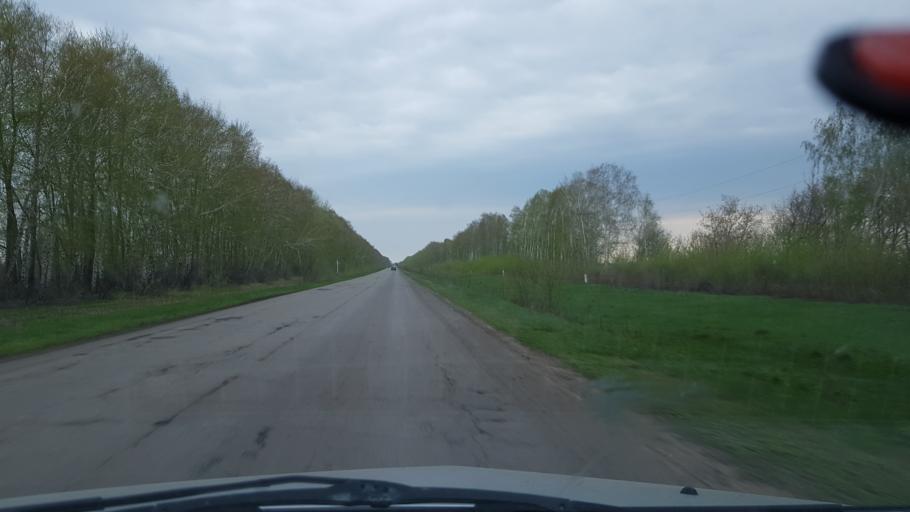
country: RU
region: Samara
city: Podstepki
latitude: 53.6614
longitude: 49.2103
